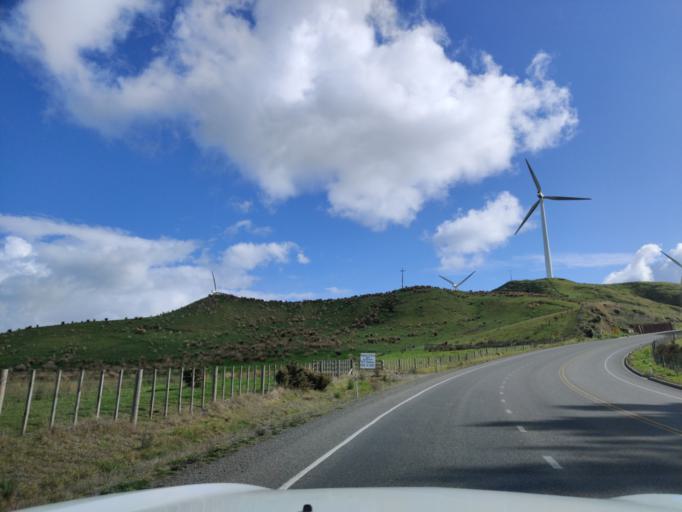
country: NZ
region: Manawatu-Wanganui
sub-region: Palmerston North City
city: Palmerston North
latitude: -40.2992
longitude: 175.8120
